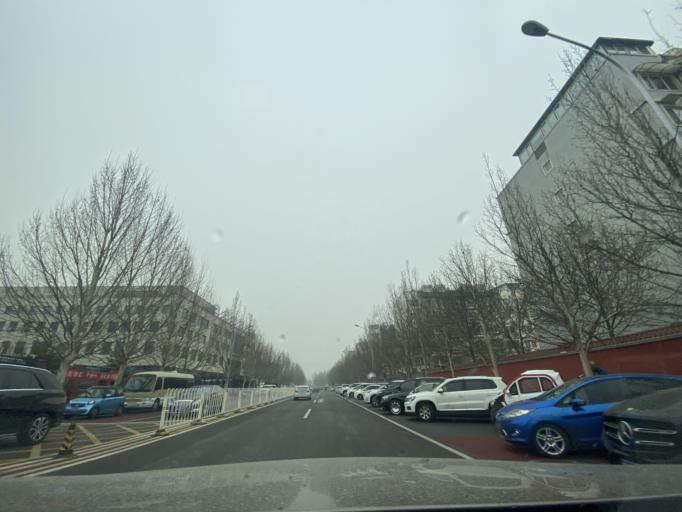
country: CN
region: Beijing
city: Sijiqing
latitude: 39.9637
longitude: 116.2418
